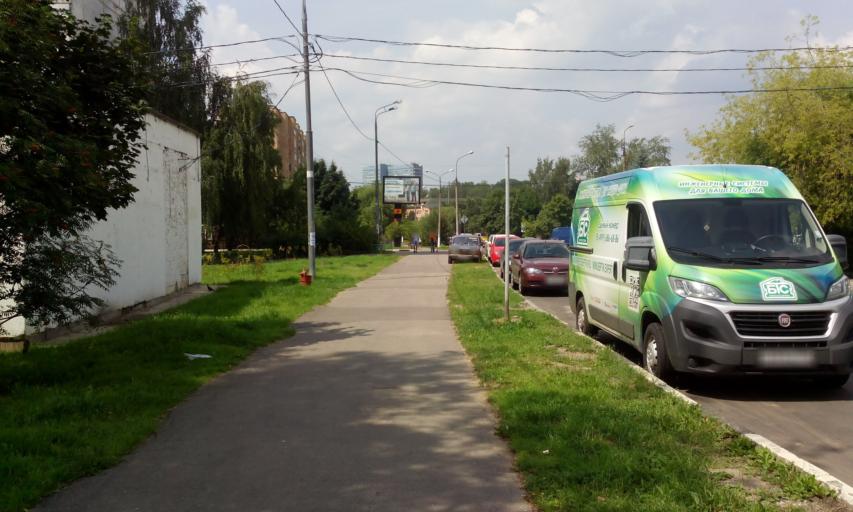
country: RU
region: Moskovskaya
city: Odintsovo
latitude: 55.6713
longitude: 37.2896
